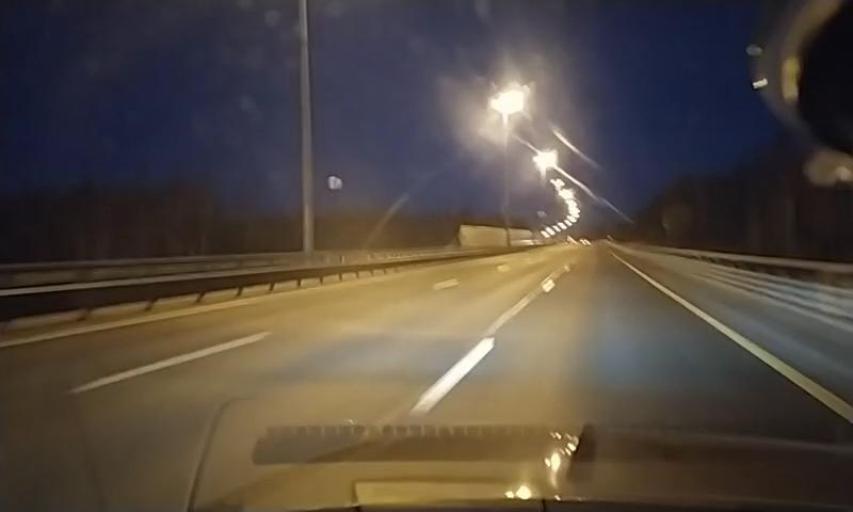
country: RU
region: St.-Petersburg
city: Pesochnyy
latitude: 60.1095
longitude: 30.0836
